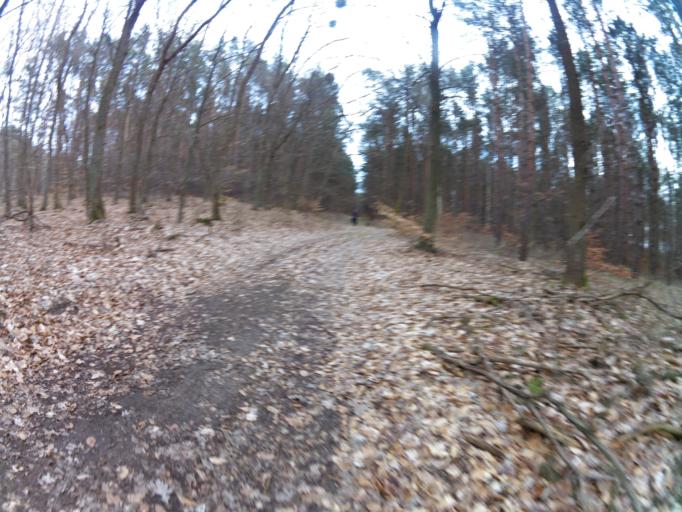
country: PL
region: Lubusz
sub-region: Powiat gorzowski
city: Lubiszyn
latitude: 52.7773
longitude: 14.8365
